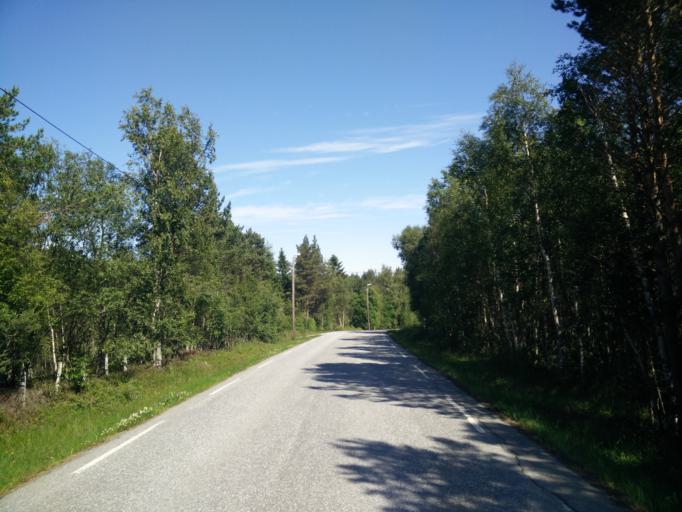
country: NO
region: More og Romsdal
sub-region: Kristiansund
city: Rensvik
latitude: 63.0652
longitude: 7.8691
